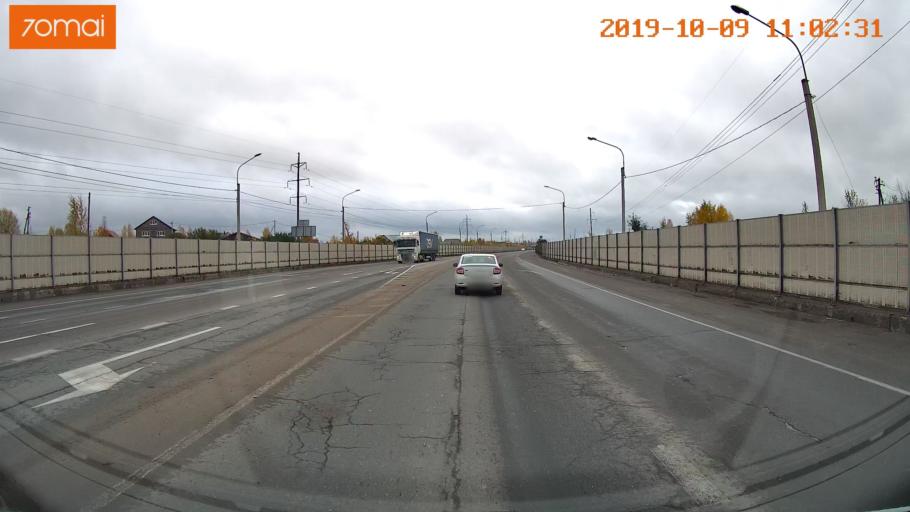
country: RU
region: Vologda
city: Vologda
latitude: 59.2318
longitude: 39.7742
